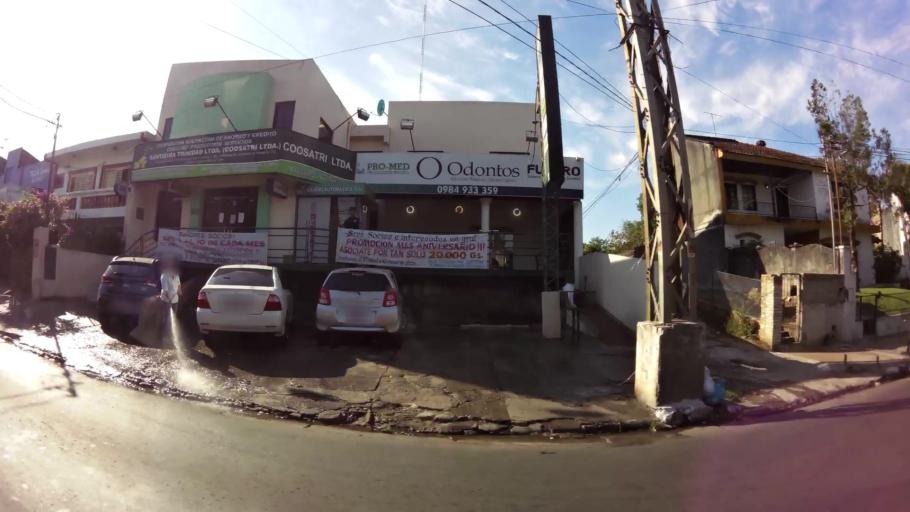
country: PY
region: Asuncion
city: Asuncion
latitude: -25.2617
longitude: -57.5911
